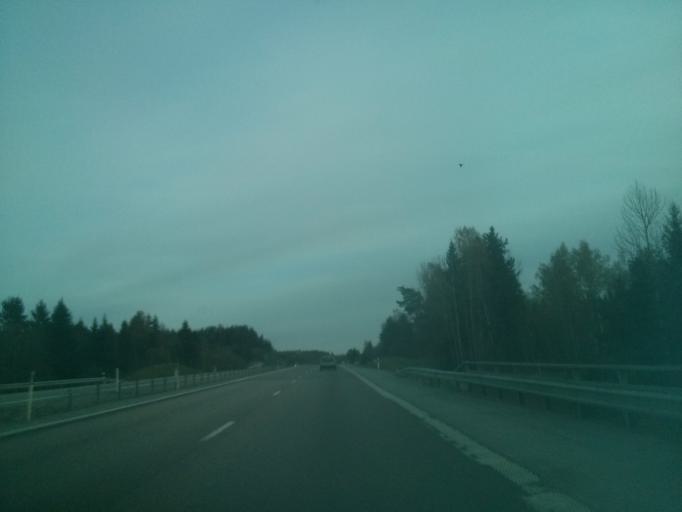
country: SE
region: Vaesternorrland
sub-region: Sundsvalls Kommun
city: Sundsbruk
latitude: 62.4342
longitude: 17.3412
